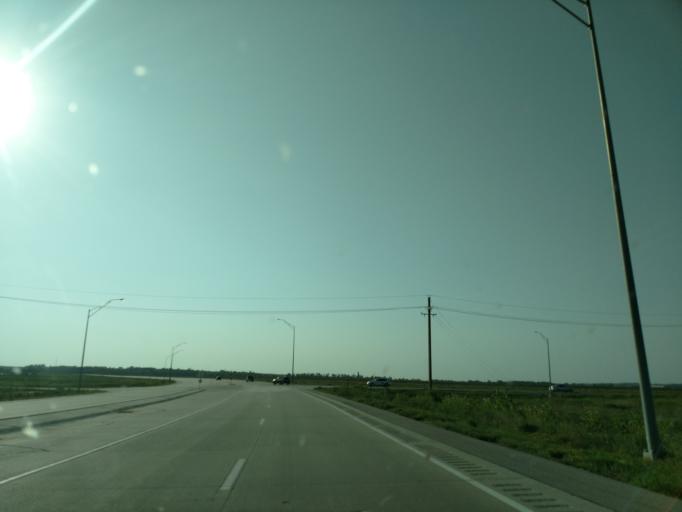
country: US
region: Nebraska
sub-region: Sarpy County
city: Offutt Air Force Base
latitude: 41.0762
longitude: -95.8902
